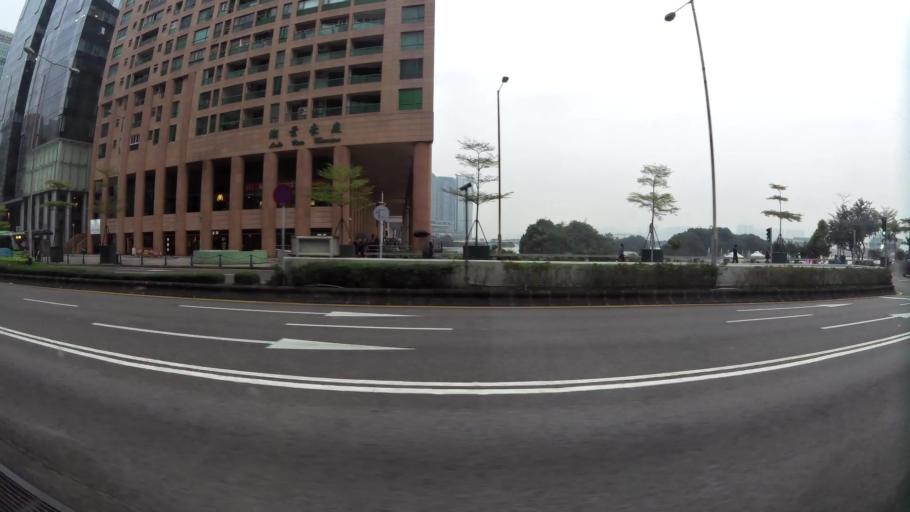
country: MO
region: Macau
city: Macau
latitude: 22.1902
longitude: 113.5387
